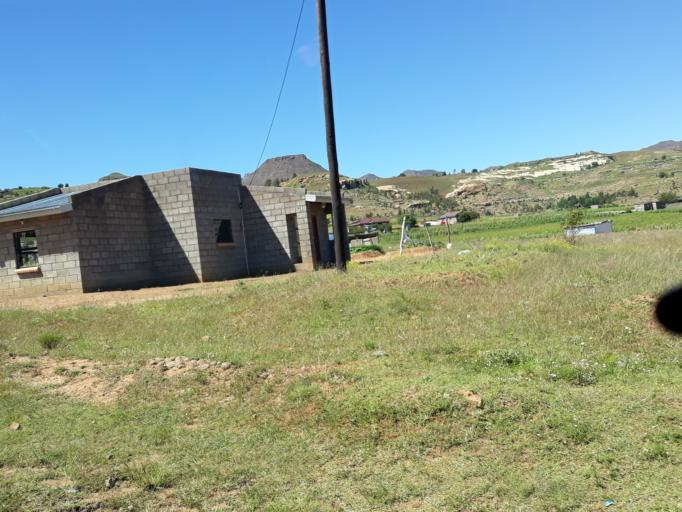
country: LS
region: Mohale's Hoek District
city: Mohale's Hoek
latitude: -30.1077
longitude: 27.4771
